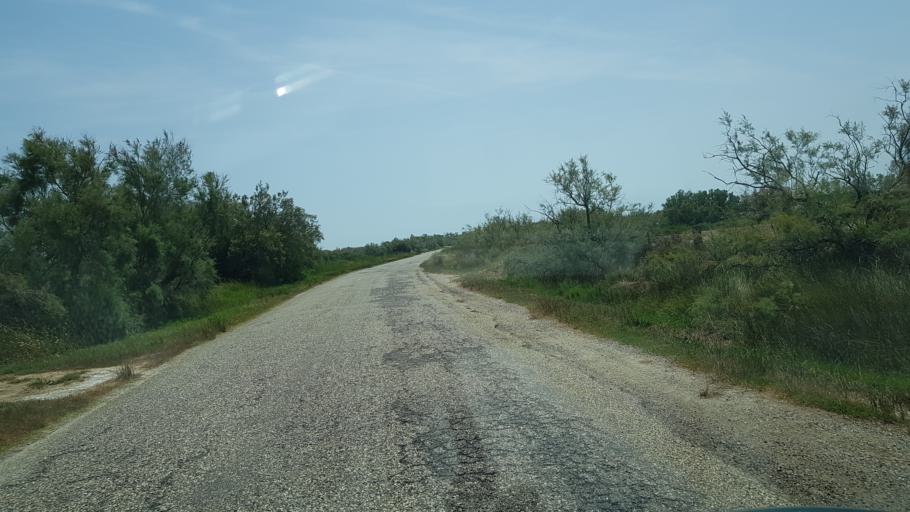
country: FR
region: Provence-Alpes-Cote d'Azur
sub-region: Departement des Bouches-du-Rhone
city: Arles
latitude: 43.5409
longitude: 4.6357
